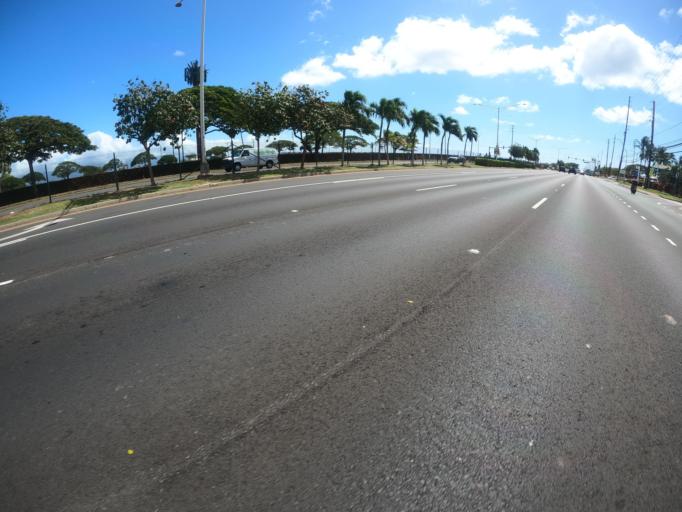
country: US
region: Hawaii
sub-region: Honolulu County
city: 'Ewa Gentry
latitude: 21.3490
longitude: -158.0273
